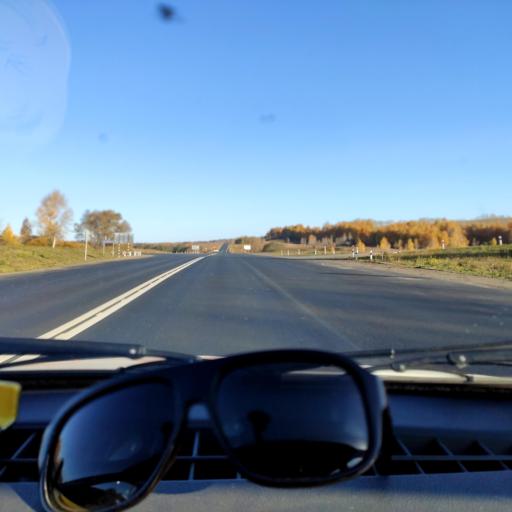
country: RU
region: Bashkortostan
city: Blagoveshchensk
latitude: 55.1097
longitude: 55.8419
